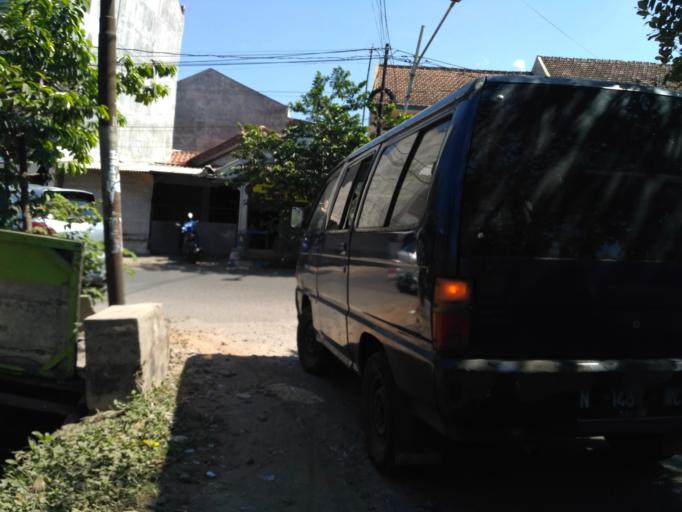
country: ID
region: East Java
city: Malang
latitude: -7.9727
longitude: 112.6671
